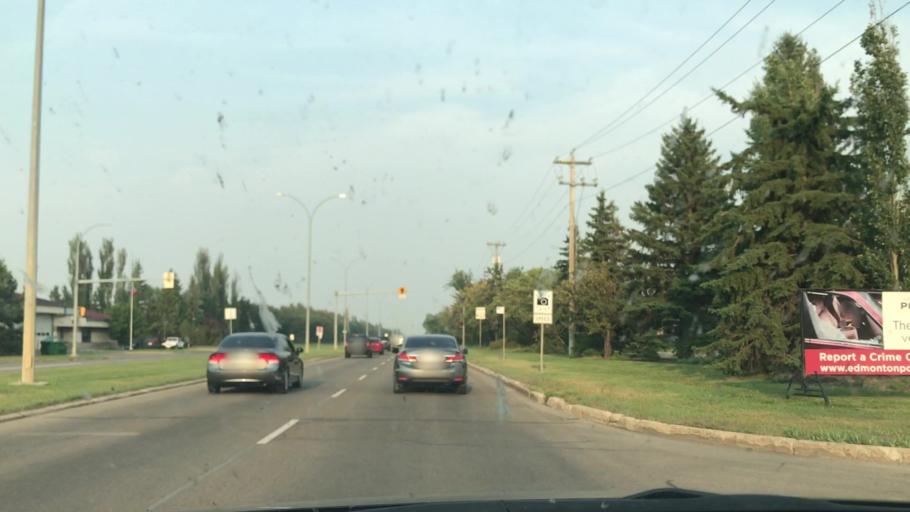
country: CA
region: Alberta
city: Edmonton
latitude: 53.5996
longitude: -113.4667
